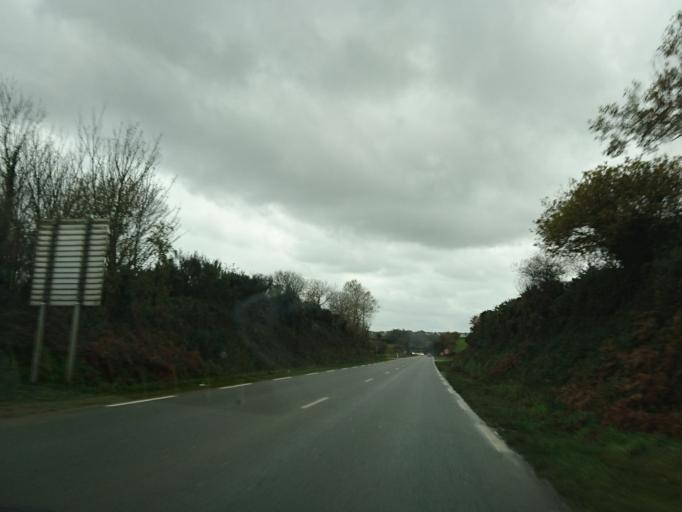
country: FR
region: Brittany
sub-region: Departement du Finistere
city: Plouzane
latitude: 48.3721
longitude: -4.5650
